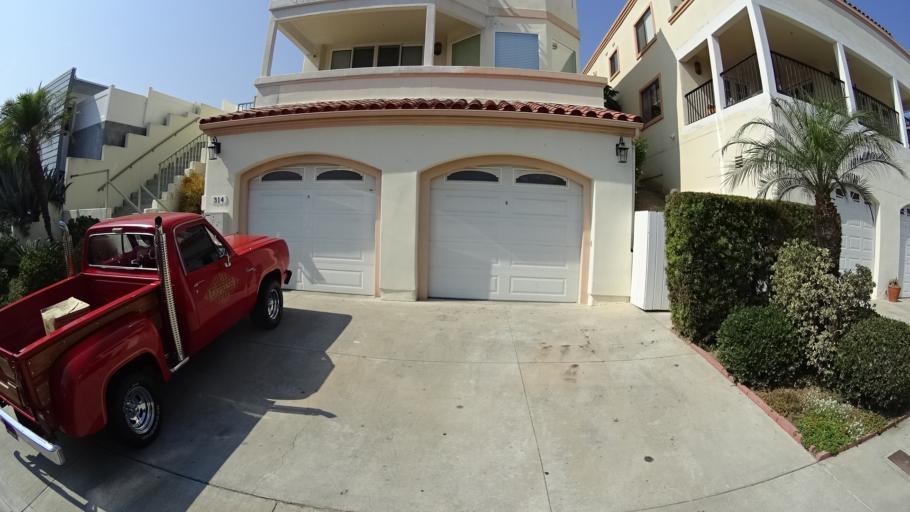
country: US
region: California
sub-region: Orange County
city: San Clemente
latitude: 33.4200
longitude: -117.6151
